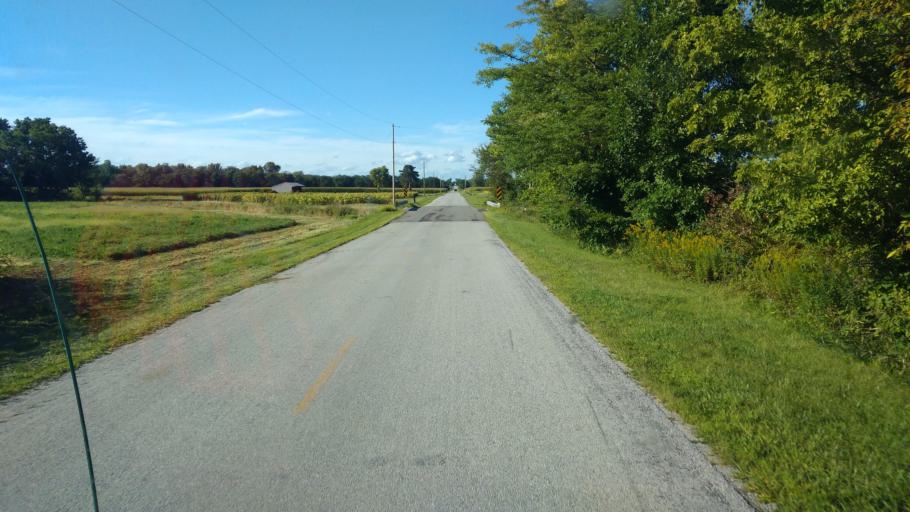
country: US
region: Ohio
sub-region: Hardin County
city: Forest
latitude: 40.7560
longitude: -83.5763
